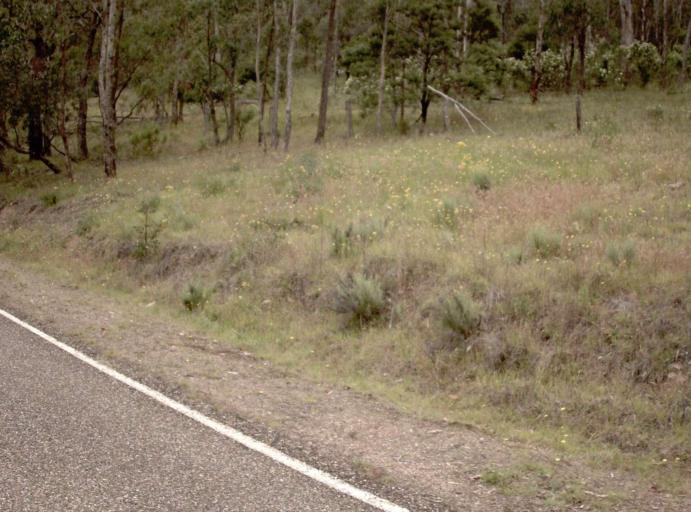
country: AU
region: Victoria
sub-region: East Gippsland
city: Bairnsdale
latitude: -37.5376
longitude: 147.2097
